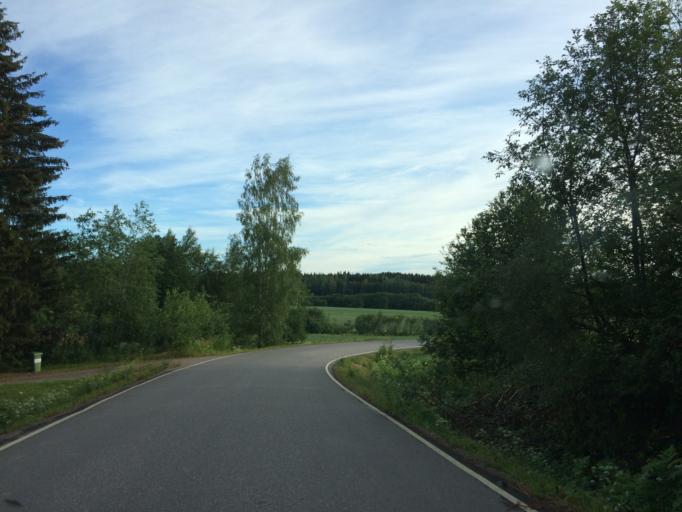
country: FI
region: Haeme
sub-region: Haemeenlinna
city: Janakkala
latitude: 60.8677
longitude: 24.5535
